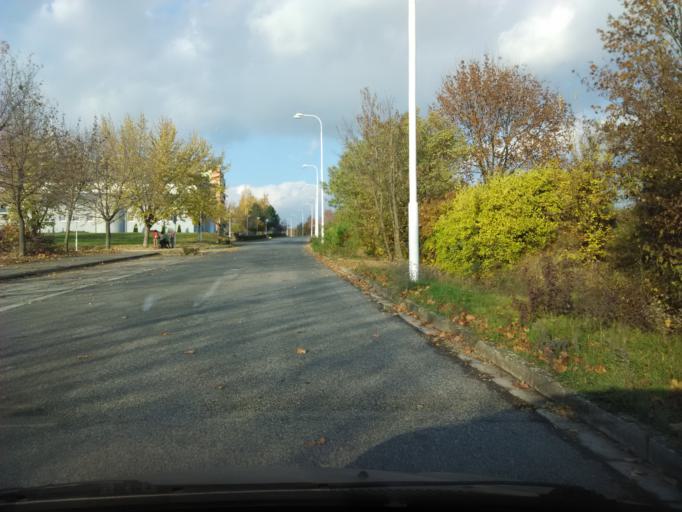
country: SK
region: Nitriansky
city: Tlmace
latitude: 48.2940
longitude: 18.5220
